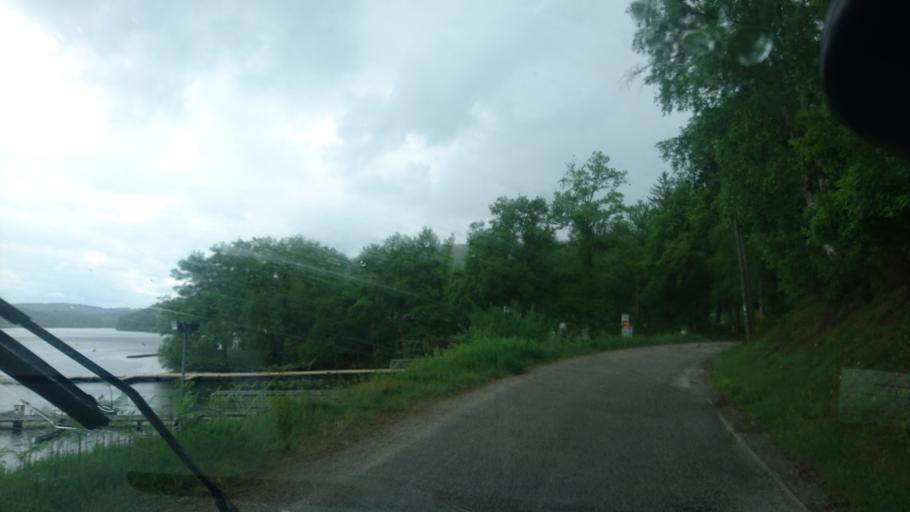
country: FR
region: Limousin
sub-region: Departement de la Haute-Vienne
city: Peyrat-le-Chateau
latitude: 45.8010
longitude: 1.8451
